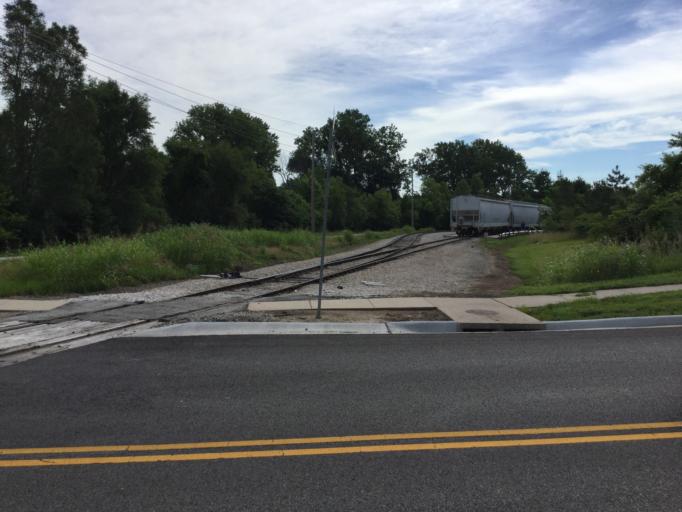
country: US
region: Kansas
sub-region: Johnson County
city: De Soto
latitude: 38.9689
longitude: -94.9772
